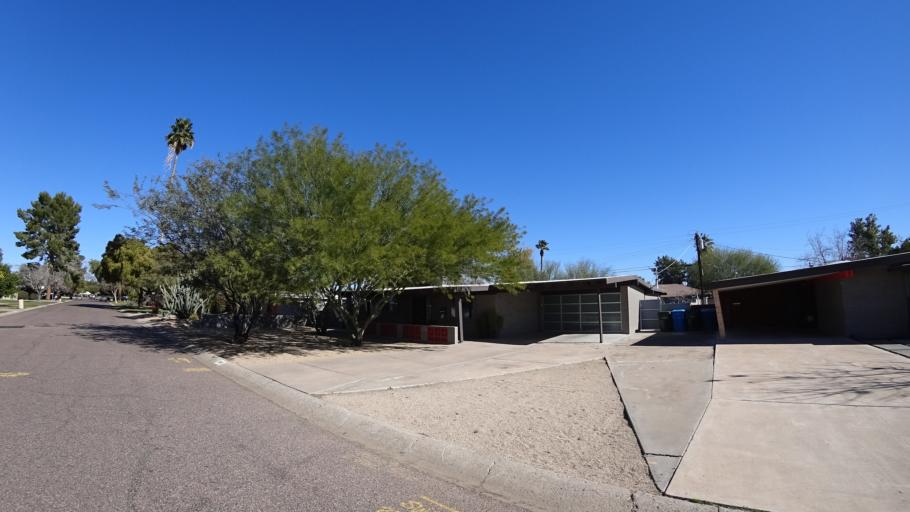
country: US
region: Arizona
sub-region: Maricopa County
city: Phoenix
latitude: 33.5204
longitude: -112.0589
